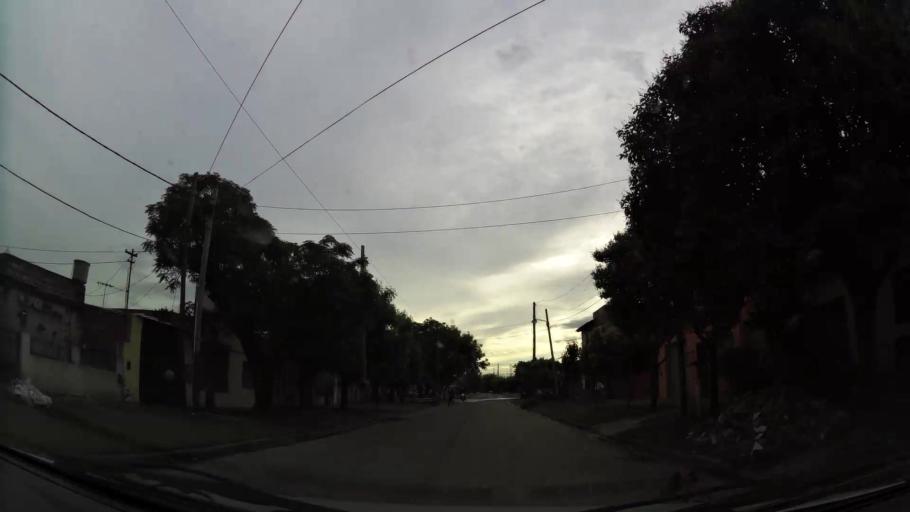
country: AR
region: Buenos Aires
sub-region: Partido de Lomas de Zamora
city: Lomas de Zamora
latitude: -34.7434
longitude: -58.3449
